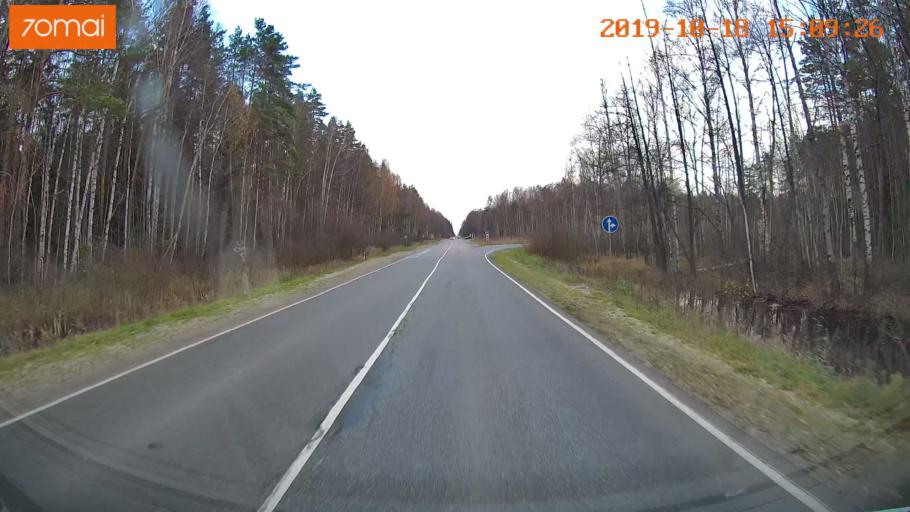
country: RU
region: Vladimir
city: Gus'-Khrustal'nyy
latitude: 55.5662
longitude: 40.6212
